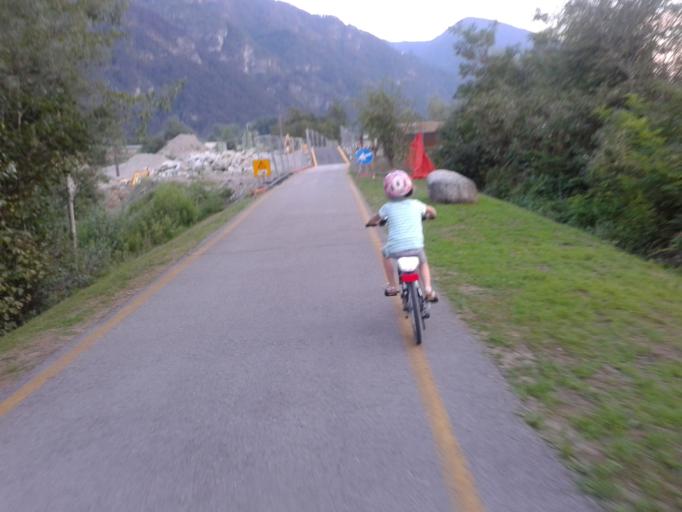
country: IT
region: Trentino-Alto Adige
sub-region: Provincia di Trento
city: Lodrone-Darzo
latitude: 45.8317
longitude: 10.5521
